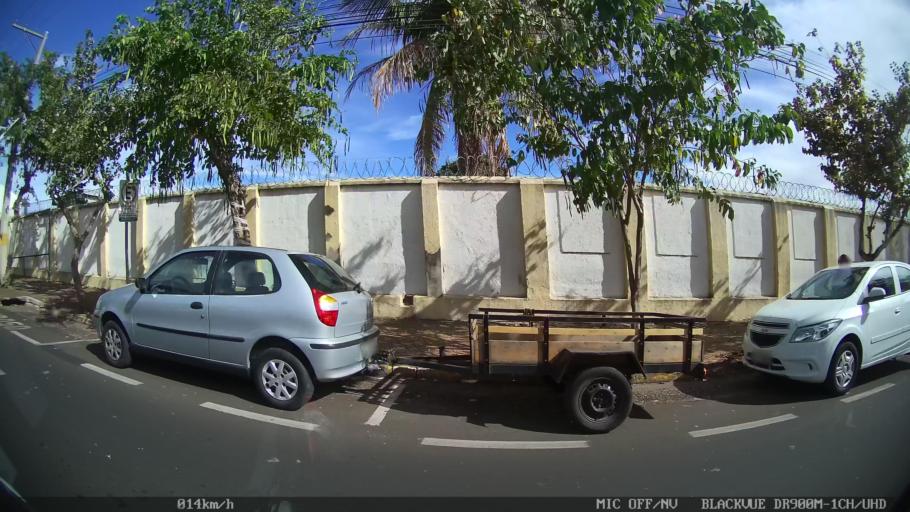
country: BR
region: Sao Paulo
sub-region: Catanduva
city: Catanduva
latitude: -21.1373
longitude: -48.9802
